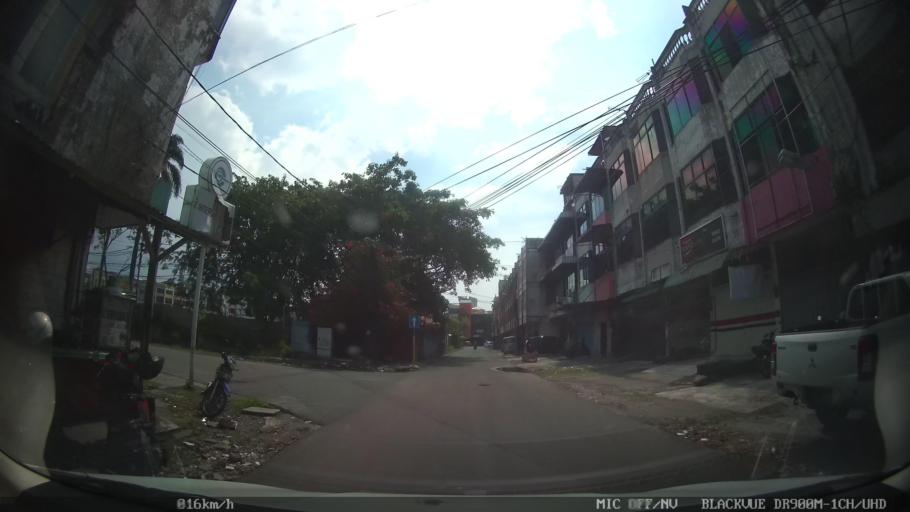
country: ID
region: North Sumatra
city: Medan
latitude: 3.5907
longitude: 98.6636
